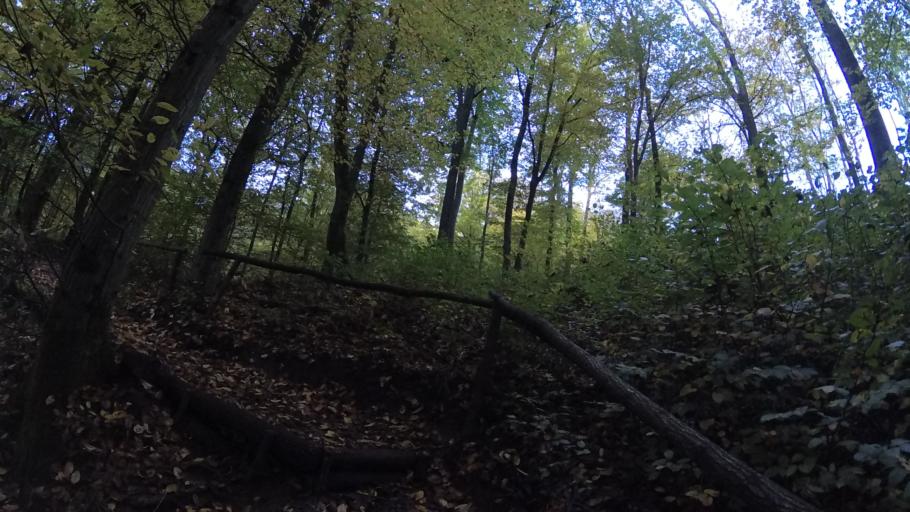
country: DE
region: Saarland
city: Sankt Wendel
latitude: 49.4561
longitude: 7.2009
